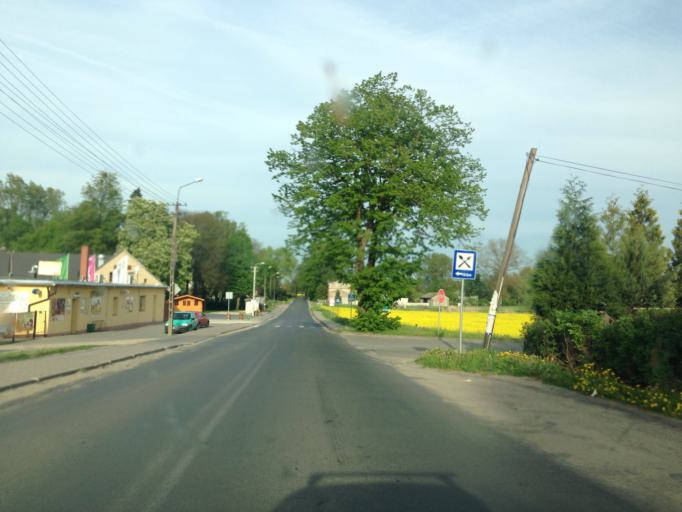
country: PL
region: Kujawsko-Pomorskie
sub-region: Powiat wabrzeski
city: Pluznica
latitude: 53.2917
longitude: 18.7798
